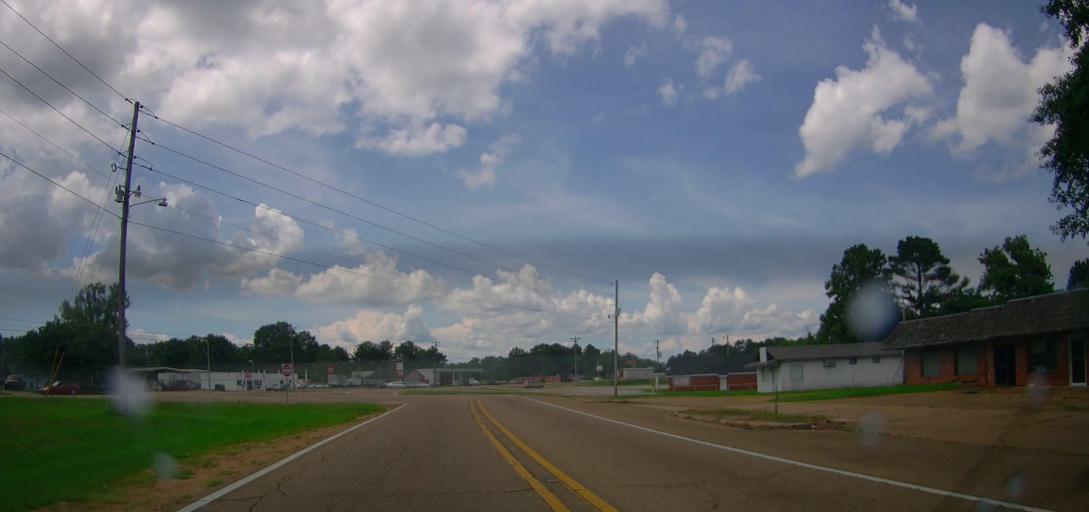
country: US
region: Mississippi
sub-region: Lee County
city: Shannon
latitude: 34.1245
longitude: -88.7187
